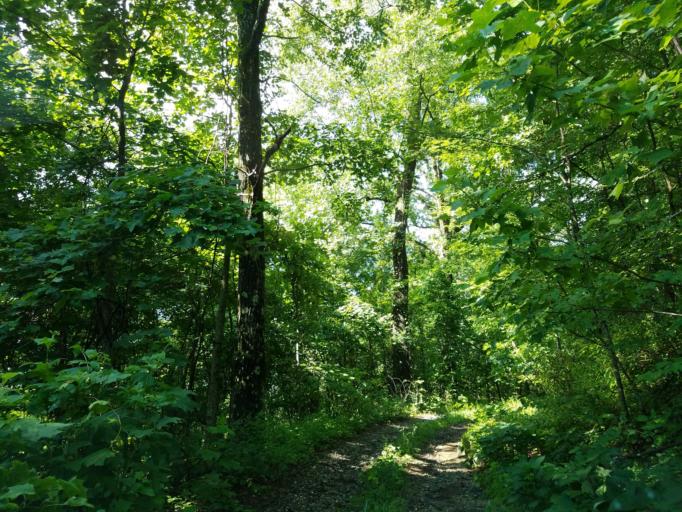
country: US
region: Georgia
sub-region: Fannin County
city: Blue Ridge
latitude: 34.6686
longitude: -84.2492
